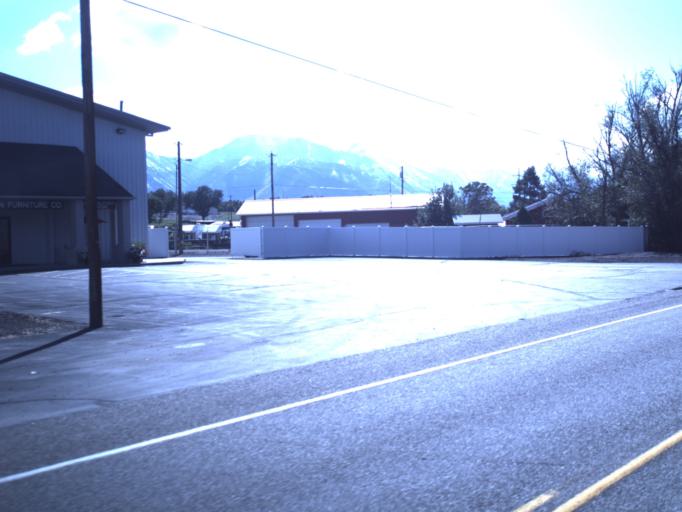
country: US
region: Utah
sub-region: Utah County
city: Springville
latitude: 40.1345
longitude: -111.6189
